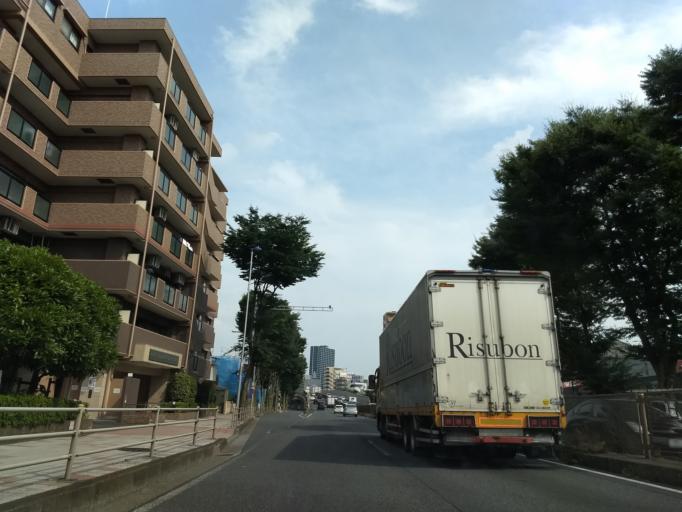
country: JP
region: Tokyo
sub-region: Machida-shi
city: Machida
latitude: 35.5374
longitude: 139.4351
